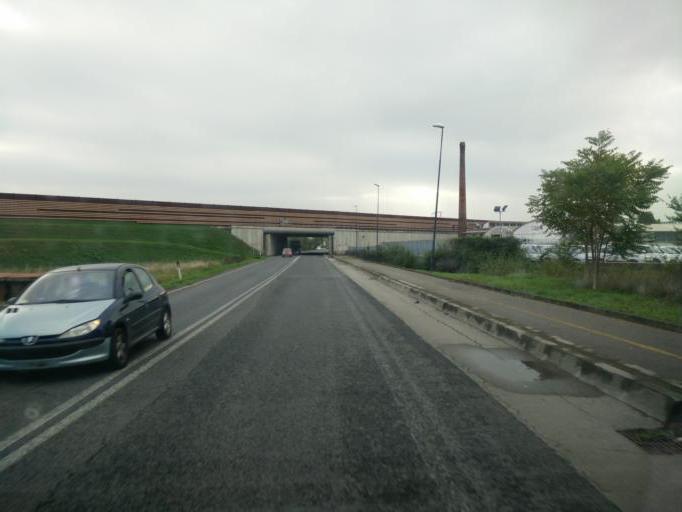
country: IT
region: Tuscany
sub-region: Province of Florence
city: Campi Bisenzio
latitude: 43.8184
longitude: 11.1500
